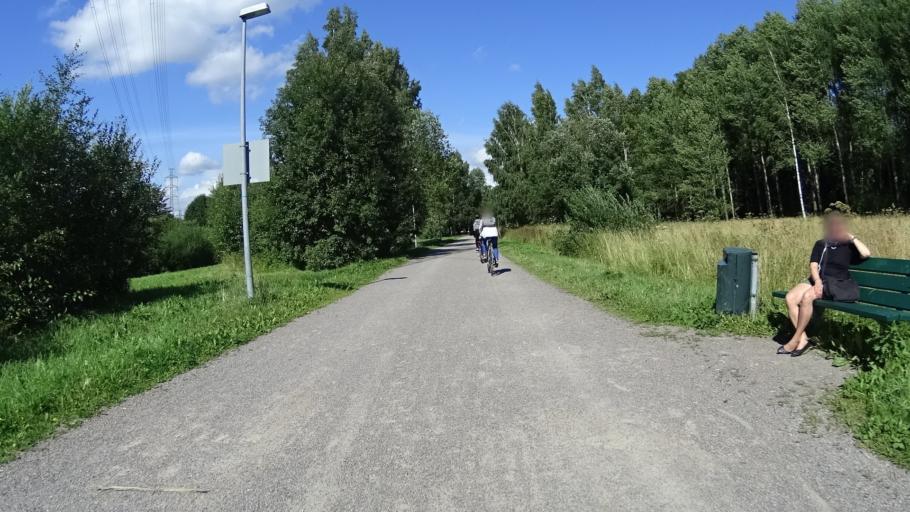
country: FI
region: Uusimaa
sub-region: Helsinki
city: Teekkarikylae
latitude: 60.2352
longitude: 24.8673
